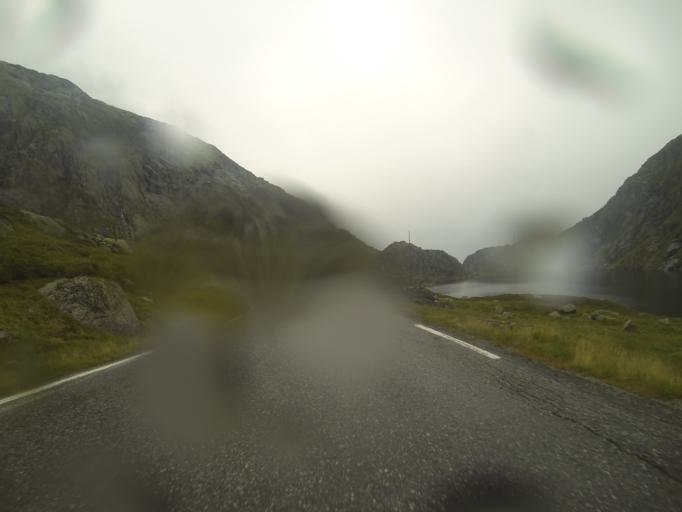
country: NO
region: Hordaland
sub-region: Odda
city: Odda
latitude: 59.7722
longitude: 6.7434
